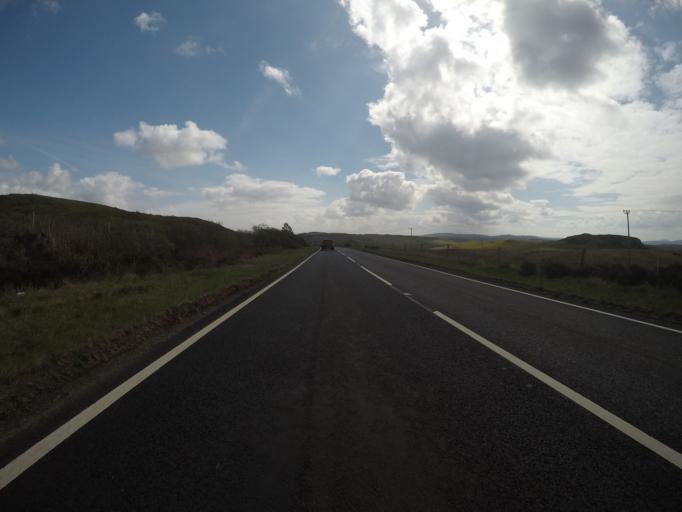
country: GB
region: Scotland
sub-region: Highland
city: Portree
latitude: 57.5369
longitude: -6.3616
